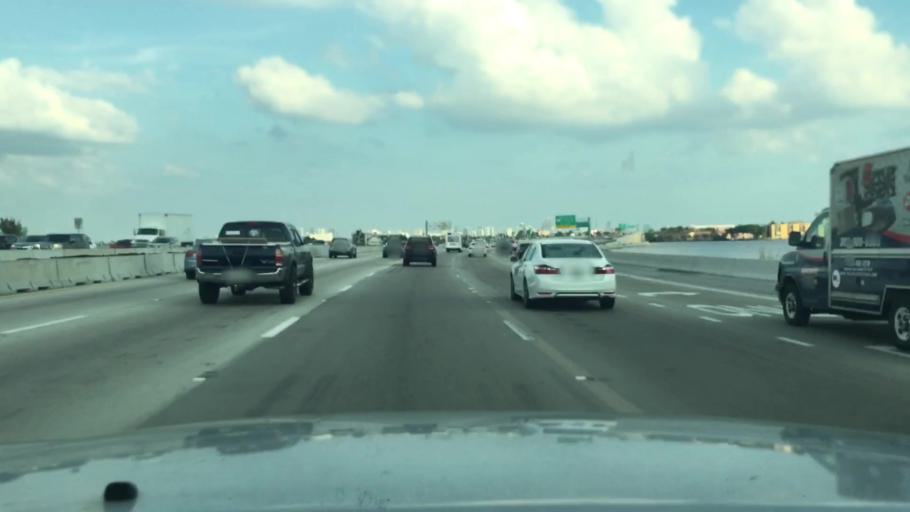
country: US
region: Florida
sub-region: Miami-Dade County
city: West Miami
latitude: 25.7850
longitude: -80.2796
